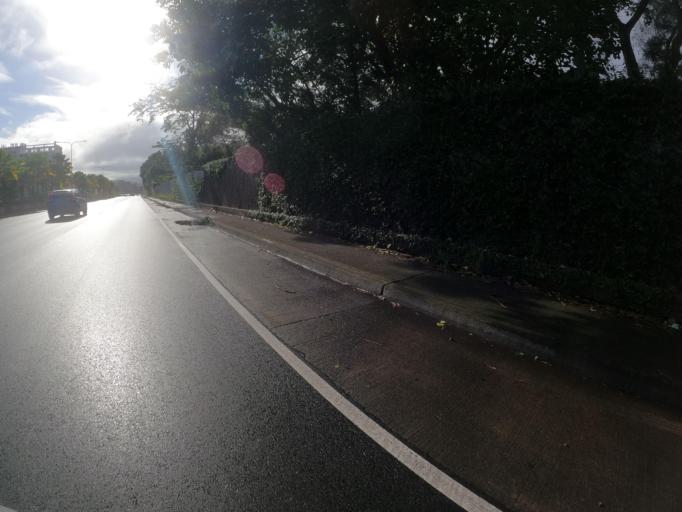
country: US
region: Hawaii
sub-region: Honolulu County
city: Kane'ohe
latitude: 21.4154
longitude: -157.8124
